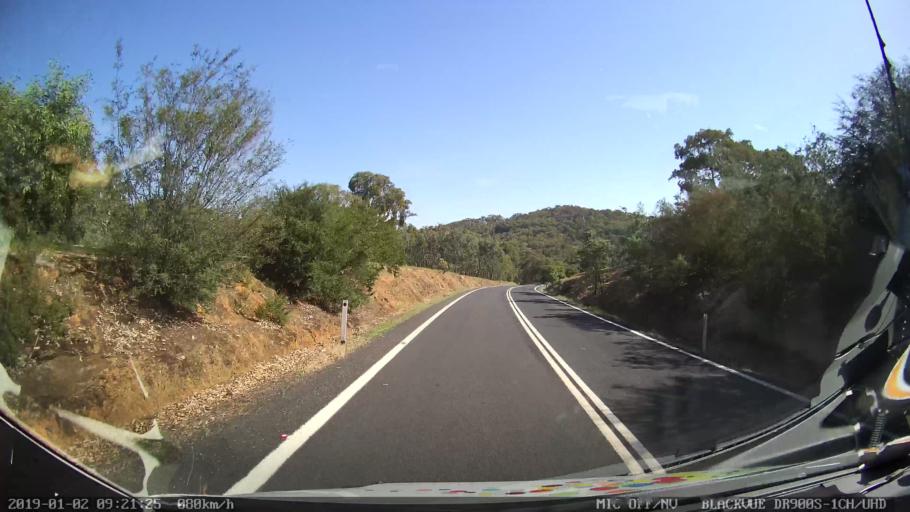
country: AU
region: New South Wales
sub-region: Tumut Shire
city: Tumut
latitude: -35.4061
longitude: 148.2913
